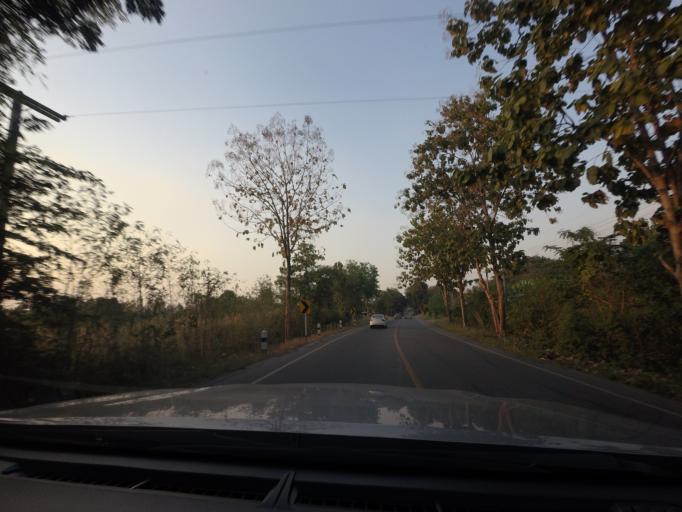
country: TH
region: Phitsanulok
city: Wang Thong
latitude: 16.7210
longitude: 100.4620
